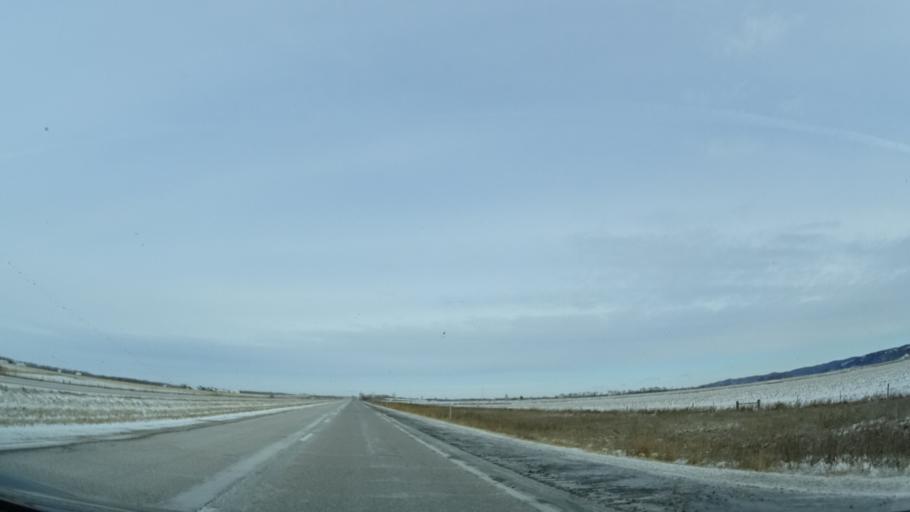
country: US
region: Nebraska
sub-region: Burt County
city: Tekamah
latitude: 41.7664
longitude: -96.0471
